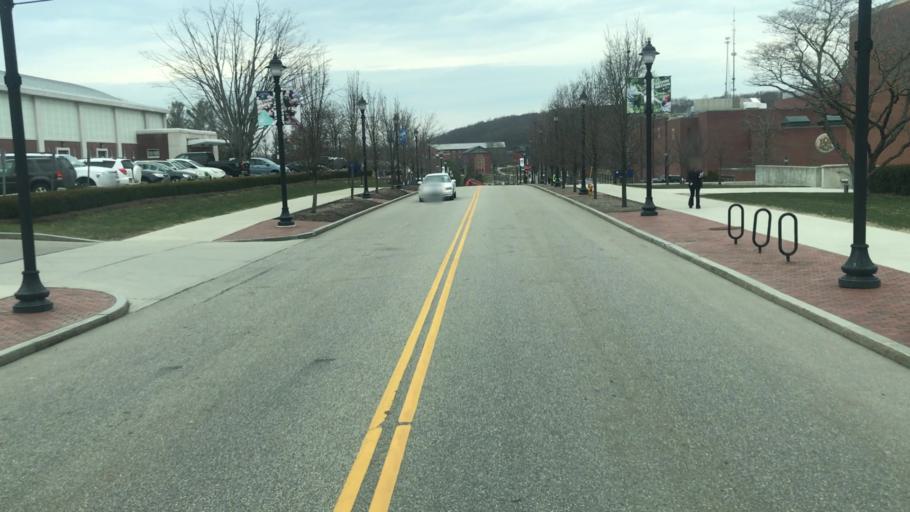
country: US
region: Connecticut
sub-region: Tolland County
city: Storrs
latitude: 41.8070
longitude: -72.2553
